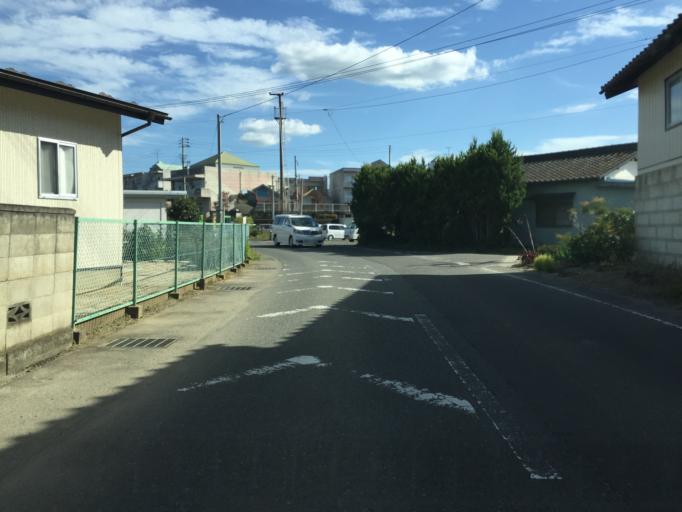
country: JP
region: Fukushima
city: Yanagawamachi-saiwaicho
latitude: 37.8388
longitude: 140.5927
